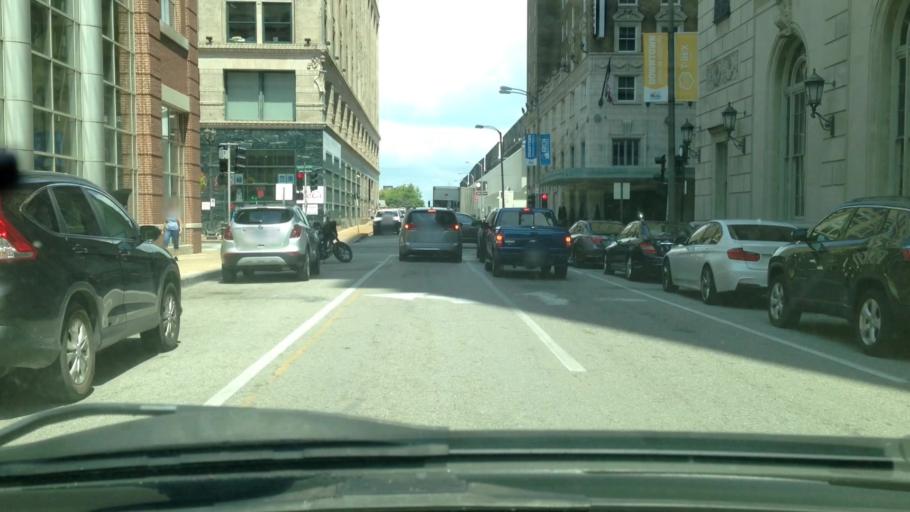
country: US
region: Missouri
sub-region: City of Saint Louis
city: St. Louis
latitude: 38.6305
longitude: -90.1928
